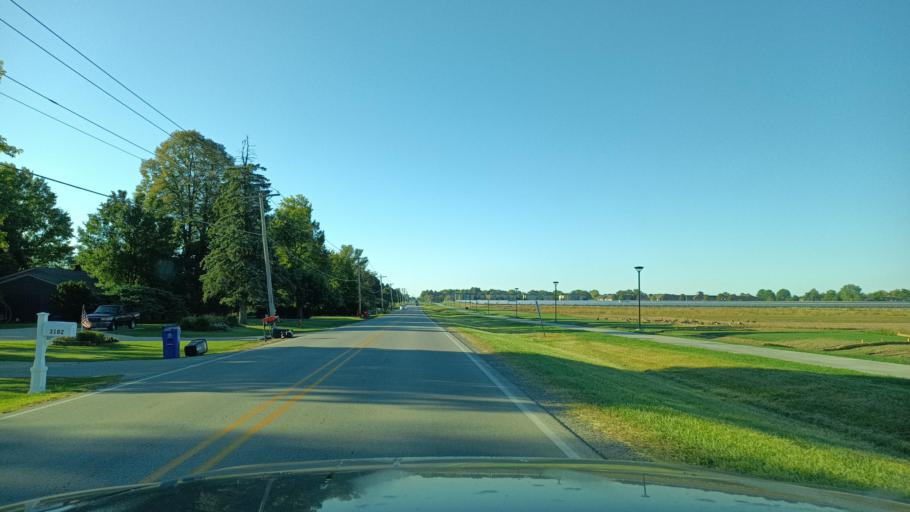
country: US
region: Illinois
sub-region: Champaign County
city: Savoy
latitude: 40.0750
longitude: -88.2385
